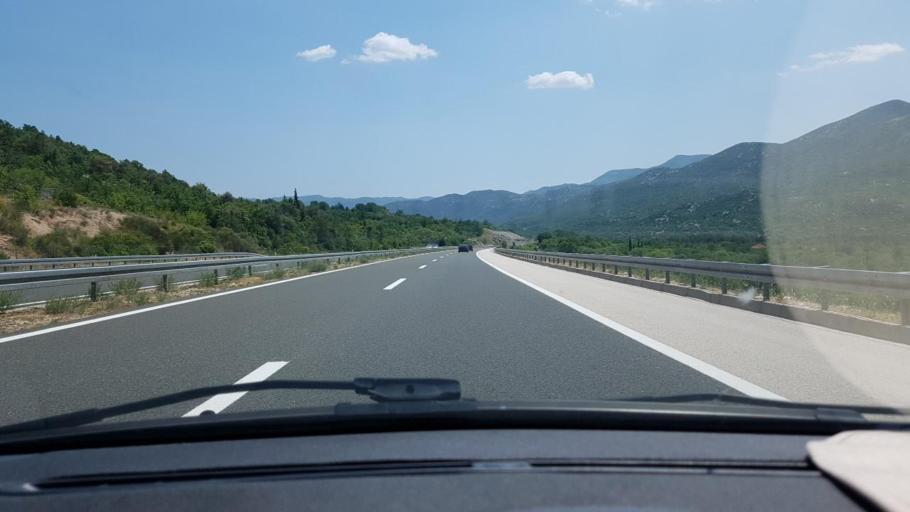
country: HR
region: Splitsko-Dalmatinska
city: Runovic
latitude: 43.2662
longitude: 17.2192
